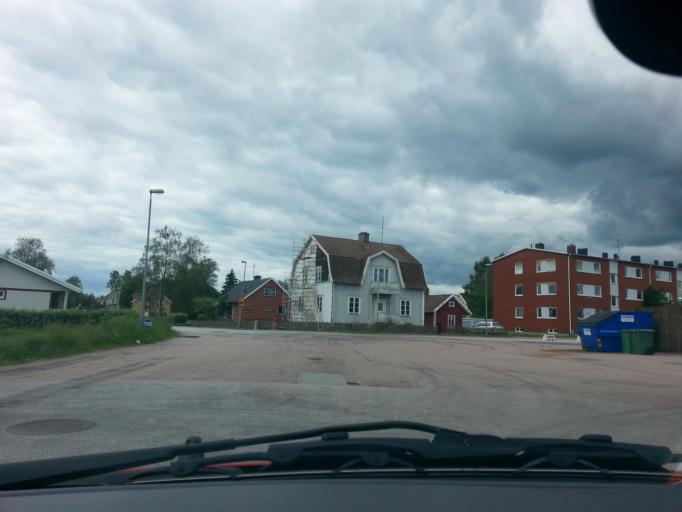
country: SE
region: Joenkoeping
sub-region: Gislaveds Kommun
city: Reftele
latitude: 57.1736
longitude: 13.5942
